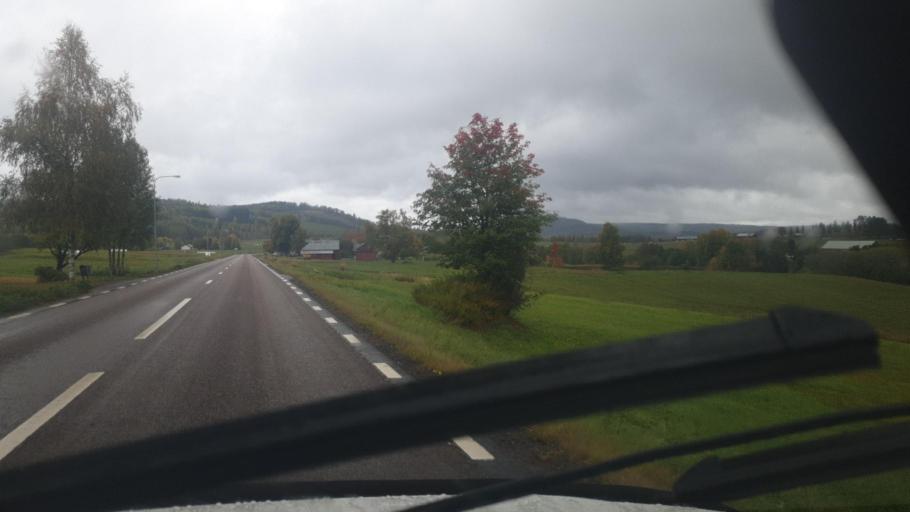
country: SE
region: Vaermland
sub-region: Sunne Kommun
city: Sunne
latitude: 59.8446
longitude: 12.9479
